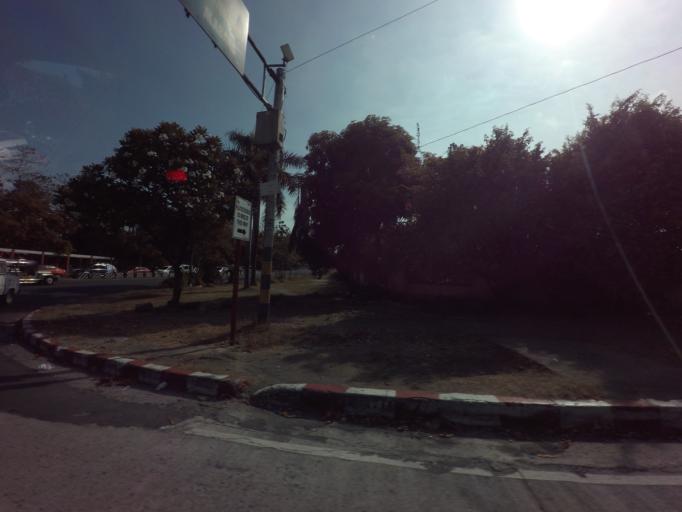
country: PH
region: Calabarzon
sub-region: Province of Rizal
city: Taguig
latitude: 14.5187
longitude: 121.0504
